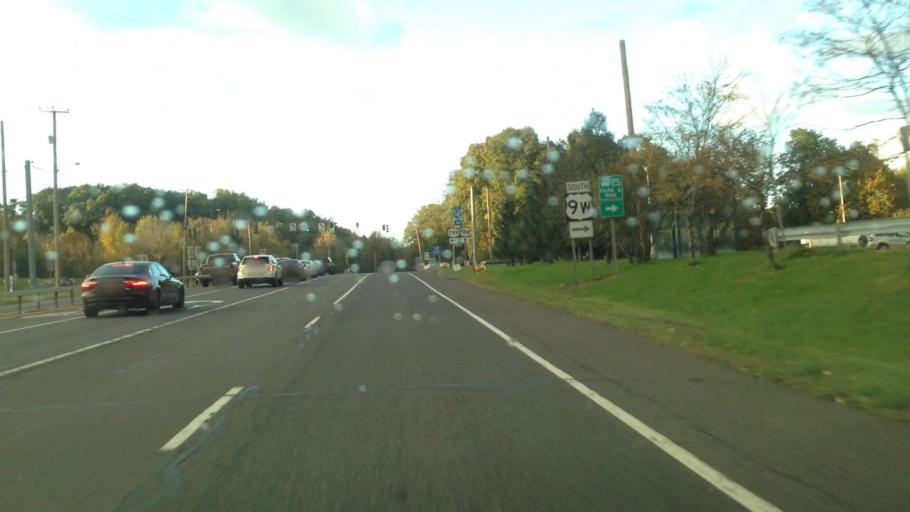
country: US
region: New York
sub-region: Ulster County
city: Highland
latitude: 41.7411
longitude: -73.9638
